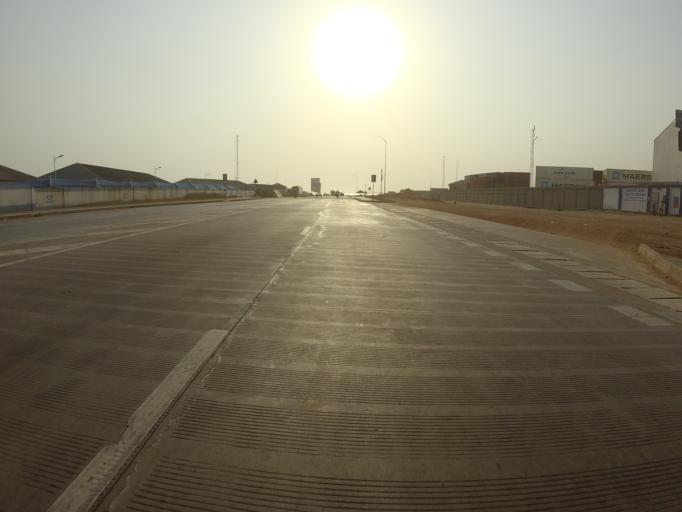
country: GH
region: Greater Accra
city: Nungua
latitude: 5.6159
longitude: -0.0254
